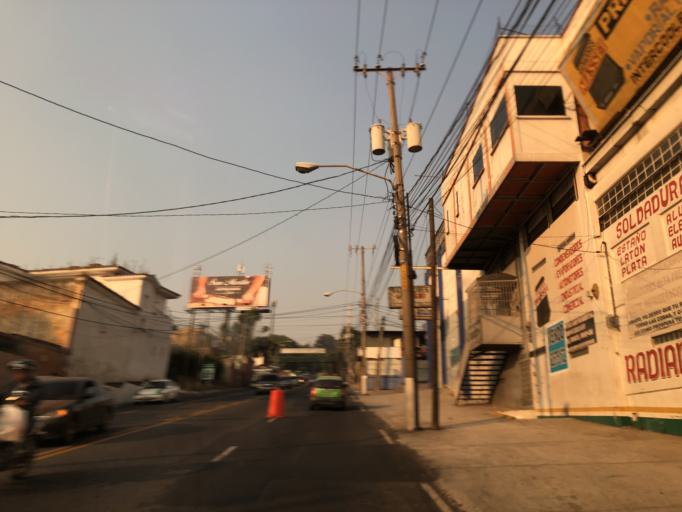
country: GT
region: Guatemala
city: Santa Catarina Pinula
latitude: 14.5646
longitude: -90.5287
